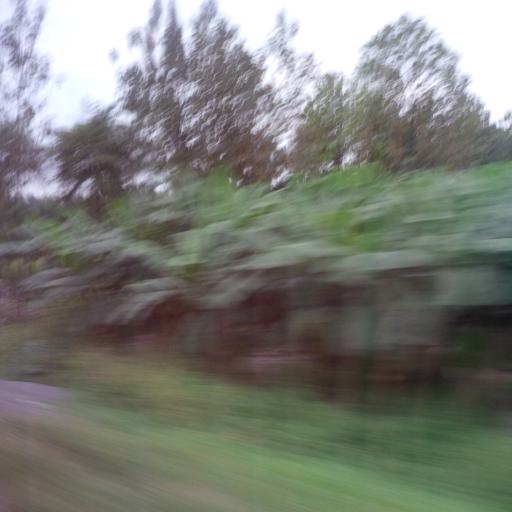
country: EC
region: Canar
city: La Troncal
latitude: -2.3432
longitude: -79.3741
